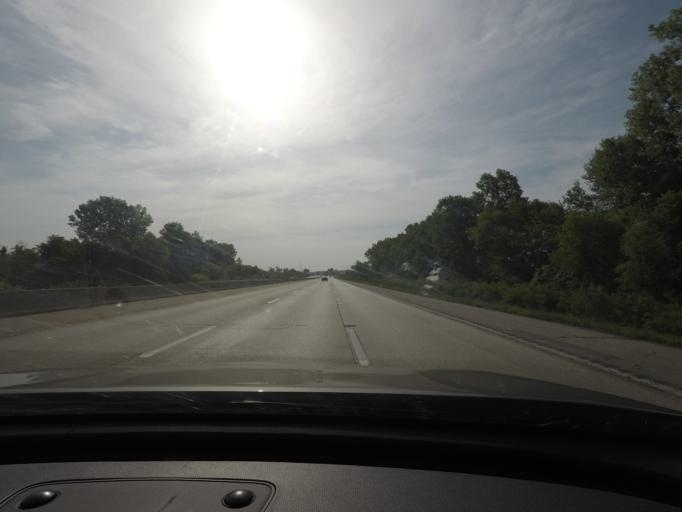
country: US
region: Missouri
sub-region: Saint Louis County
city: Bridgeton
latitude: 38.7905
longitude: -90.4330
